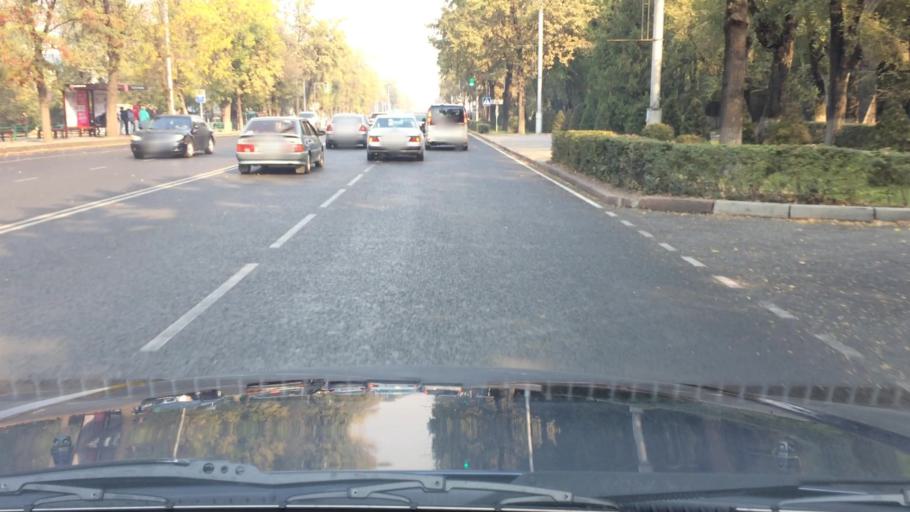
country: KG
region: Chuy
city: Bishkek
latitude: 42.8529
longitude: 74.5866
